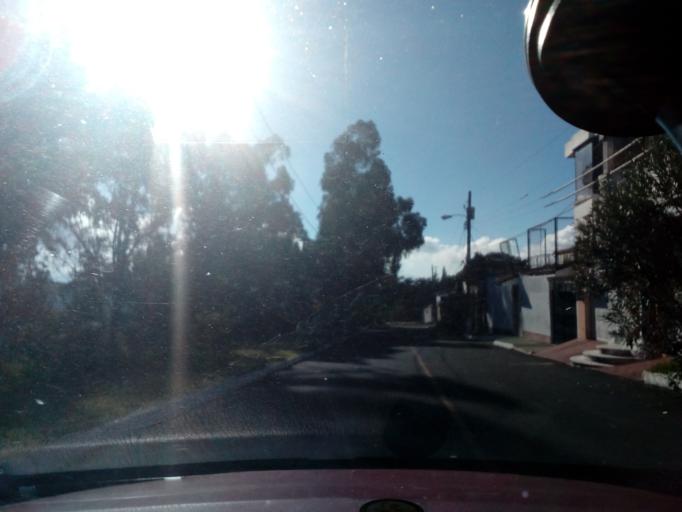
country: GT
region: Guatemala
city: Mixco
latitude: 14.6020
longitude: -90.5766
